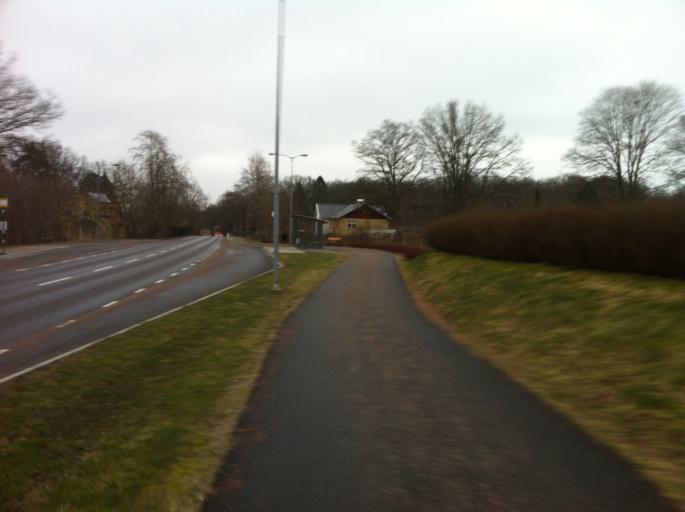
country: SE
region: Skane
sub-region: Hoors Kommun
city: Satofta
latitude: 55.9153
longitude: 13.5466
